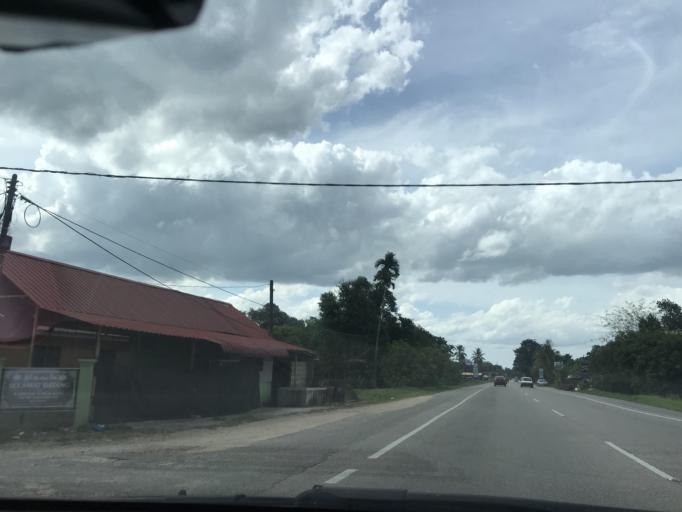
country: MY
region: Kelantan
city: Kampong Pangkal Kalong
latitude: 5.9076
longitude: 102.1873
